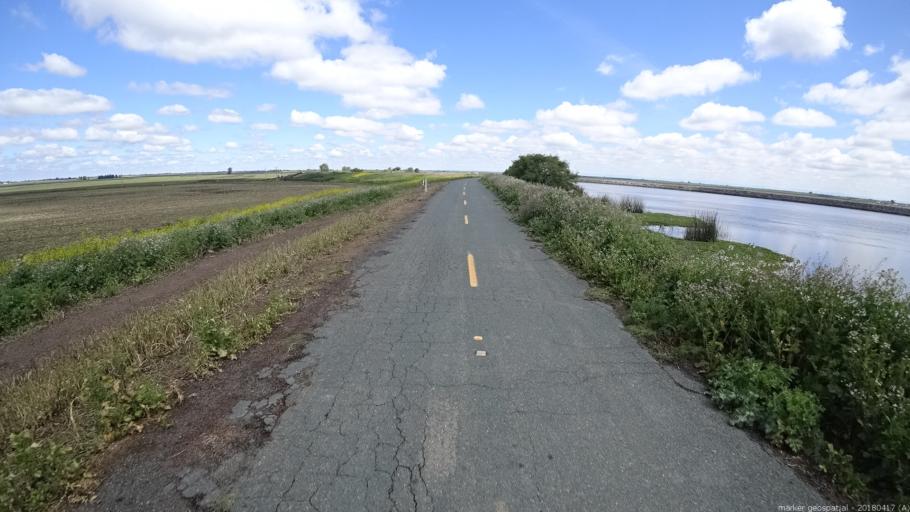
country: US
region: California
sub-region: Sacramento County
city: Walnut Grove
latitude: 38.1587
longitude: -121.5365
